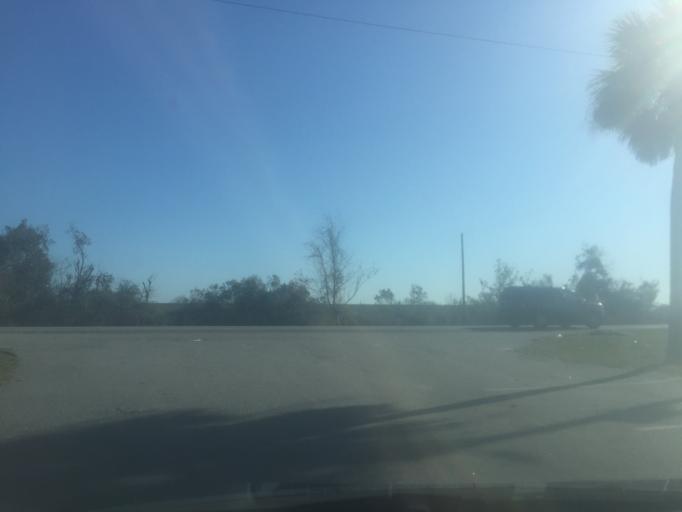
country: US
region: Georgia
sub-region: Chatham County
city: Savannah
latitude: 32.1084
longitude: -81.0828
